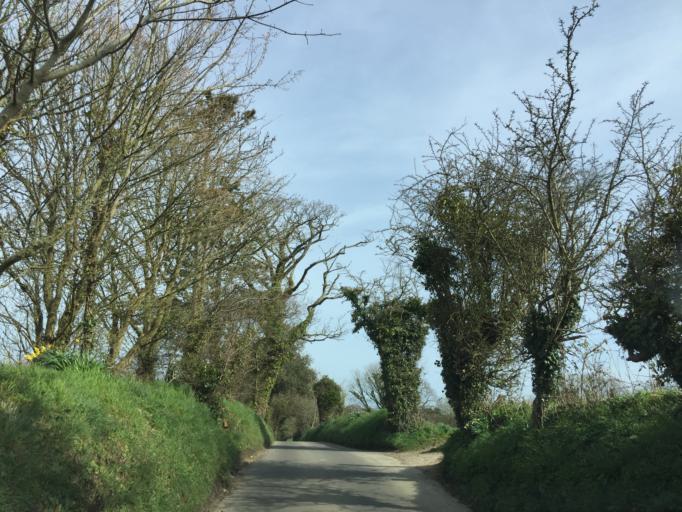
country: JE
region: St Helier
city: Saint Helier
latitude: 49.2210
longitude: -2.1395
